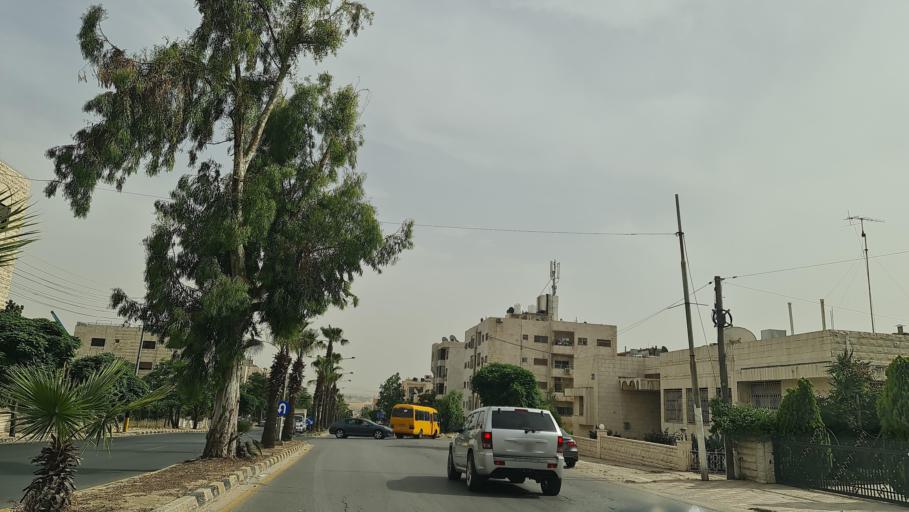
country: JO
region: Amman
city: Wadi as Sir
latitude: 31.9500
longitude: 35.8703
